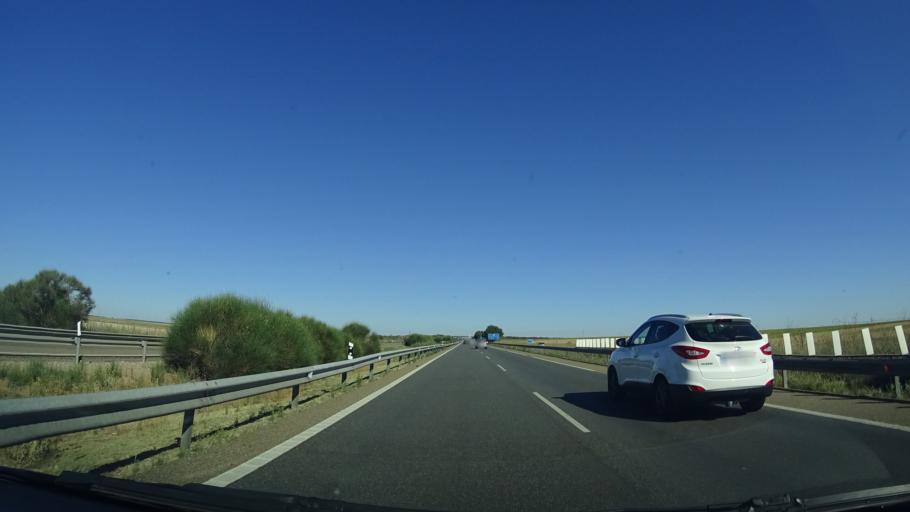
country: ES
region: Castille and Leon
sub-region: Provincia de Valladolid
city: San Pedro de Latarce
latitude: 41.7929
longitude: -5.3345
